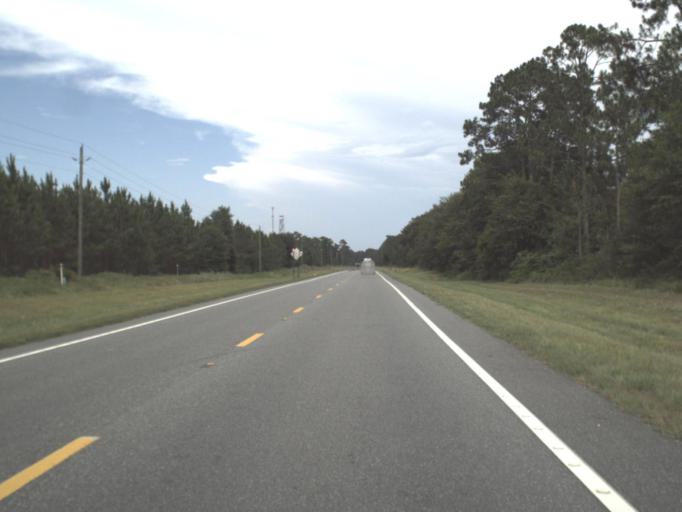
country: US
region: Florida
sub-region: Taylor County
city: Perry
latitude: 30.0997
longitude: -83.4595
